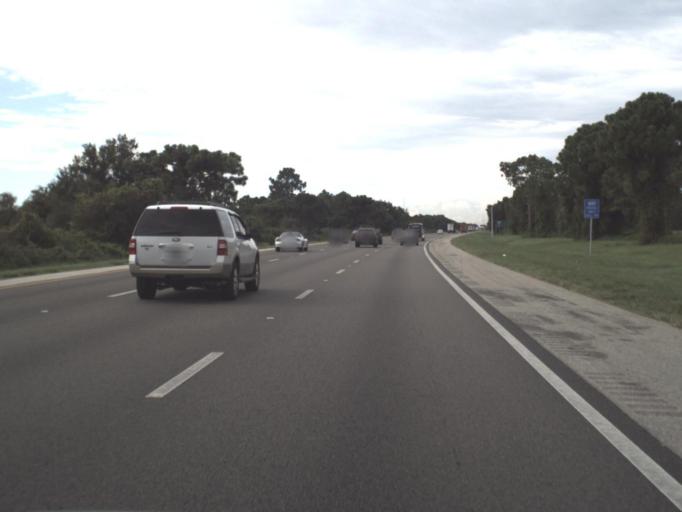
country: US
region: Florida
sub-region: Sarasota County
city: The Meadows
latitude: 27.3803
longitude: -82.4470
